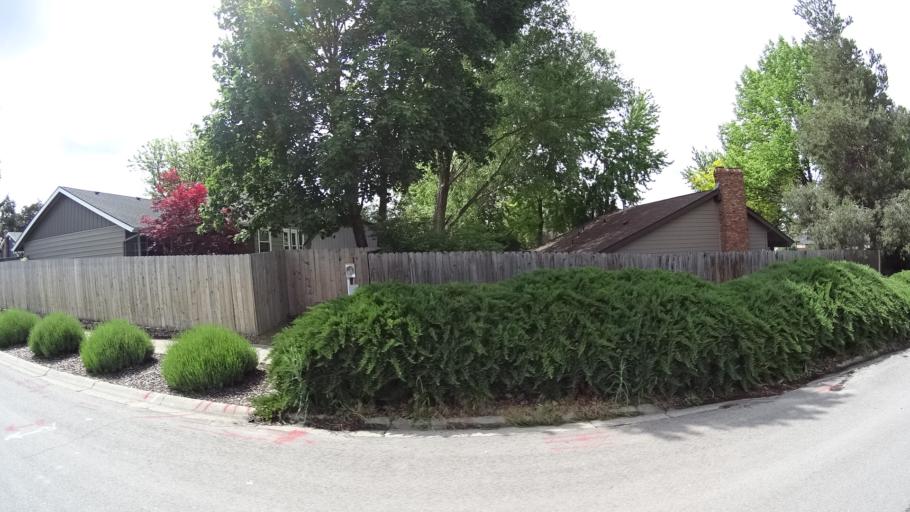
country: US
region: Idaho
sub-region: Ada County
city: Eagle
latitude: 43.7017
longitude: -116.3526
